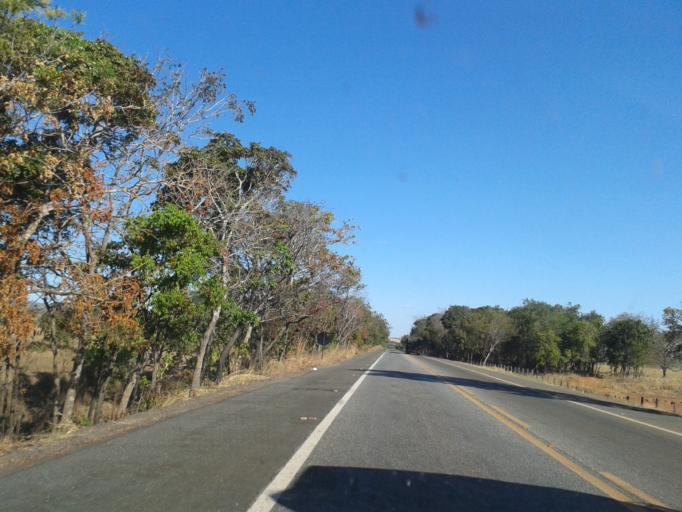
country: BR
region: Goias
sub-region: Mozarlandia
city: Mozarlandia
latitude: -14.8100
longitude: -50.5325
